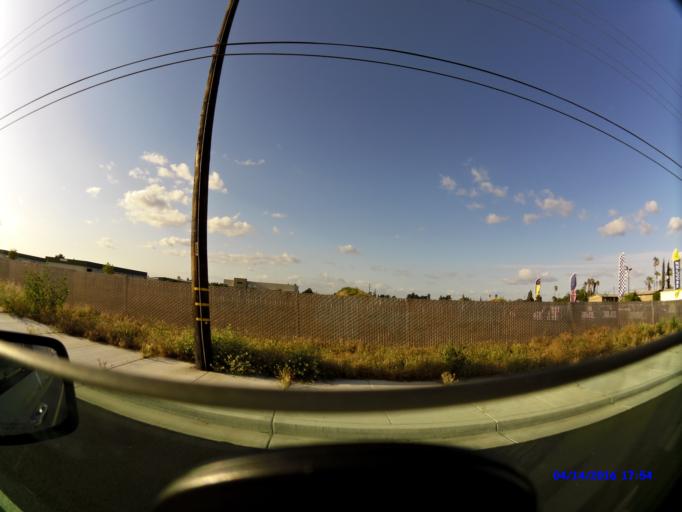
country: US
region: California
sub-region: Stanislaus County
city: Del Rio
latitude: 37.7112
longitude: -120.9973
